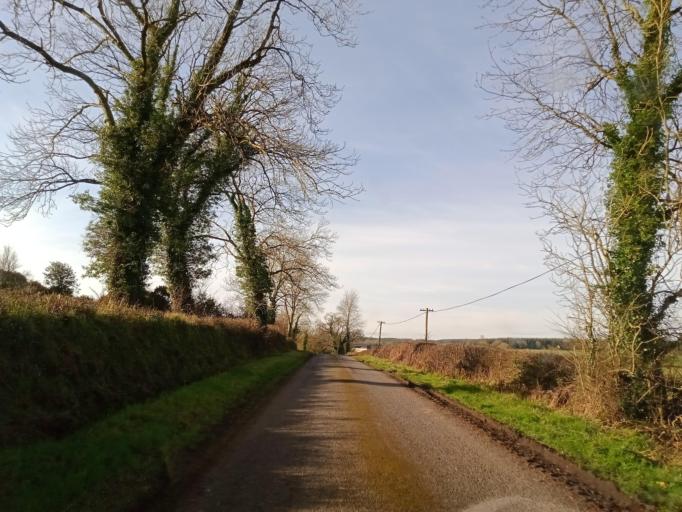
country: IE
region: Munster
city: Fethard
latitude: 52.5631
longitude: -7.5806
